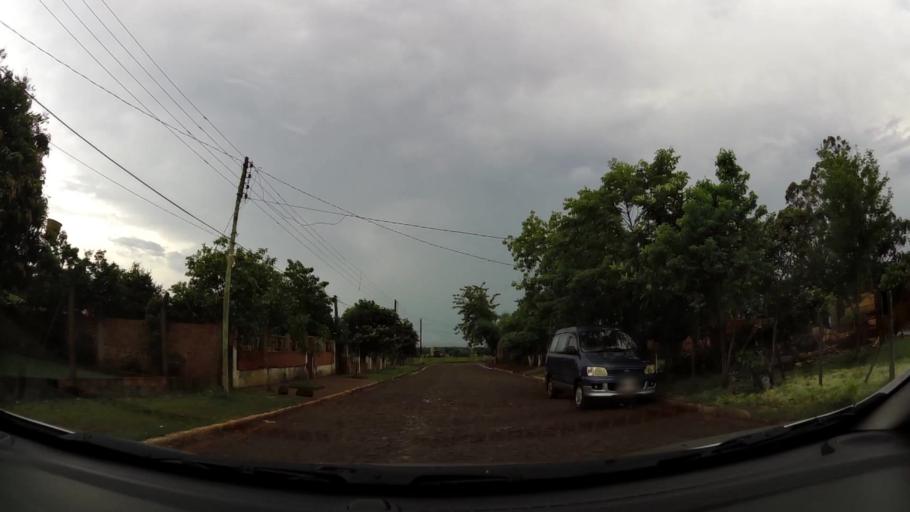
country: PY
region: Alto Parana
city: Presidente Franco
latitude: -25.5473
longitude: -54.6501
